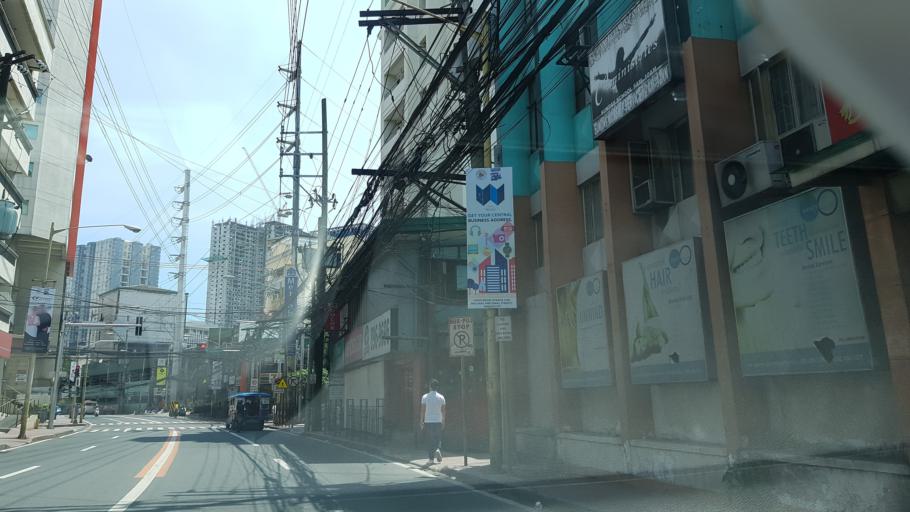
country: PH
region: Metro Manila
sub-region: Makati City
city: Makati City
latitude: 14.5631
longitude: 121.0111
